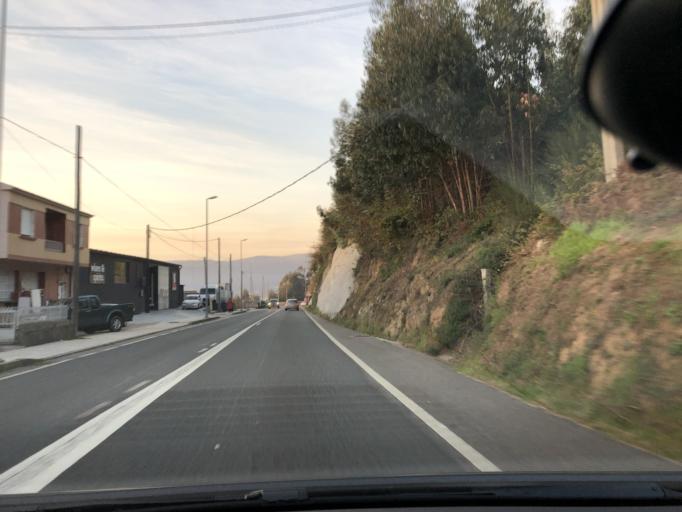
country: ES
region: Galicia
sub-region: Provincia de Pontevedra
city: Marin
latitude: 42.3893
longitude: -8.7121
